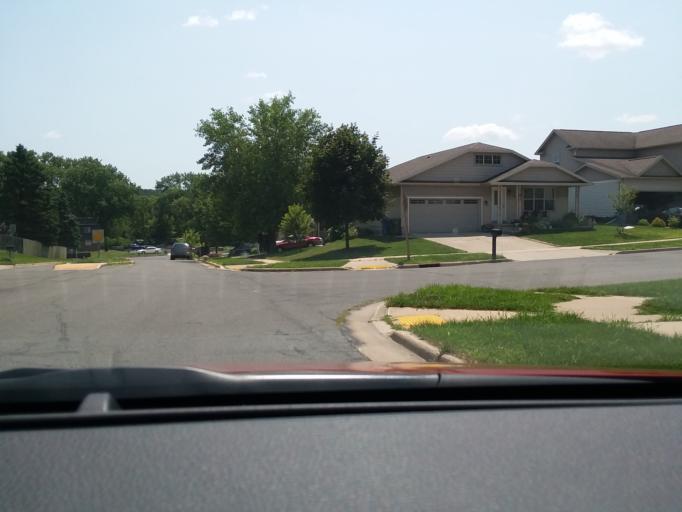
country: US
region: Wisconsin
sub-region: Dane County
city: Shorewood Hills
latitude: 43.0267
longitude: -89.4558
